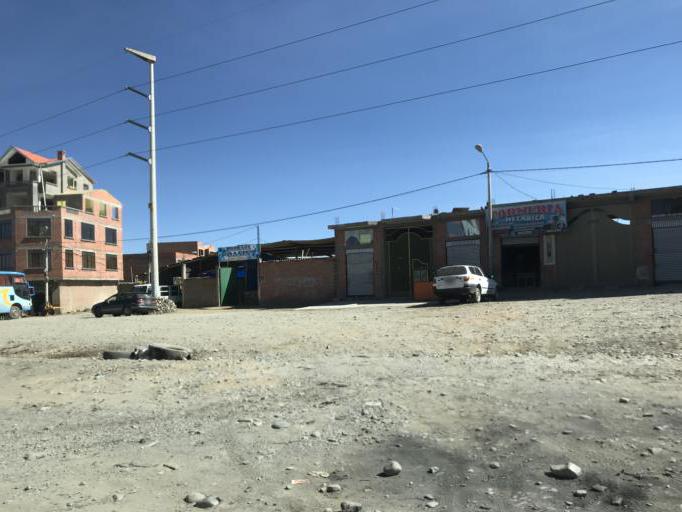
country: BO
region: La Paz
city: La Paz
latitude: -16.4995
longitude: -68.2340
